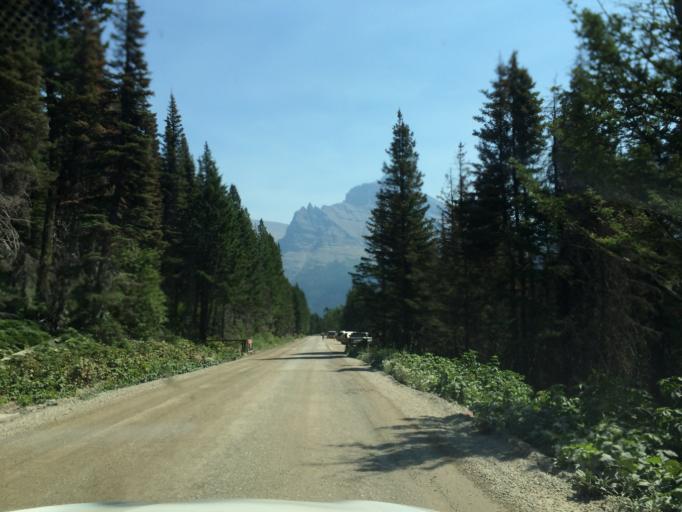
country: US
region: Montana
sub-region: Flathead County
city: Columbia Falls
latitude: 48.6791
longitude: -113.6555
